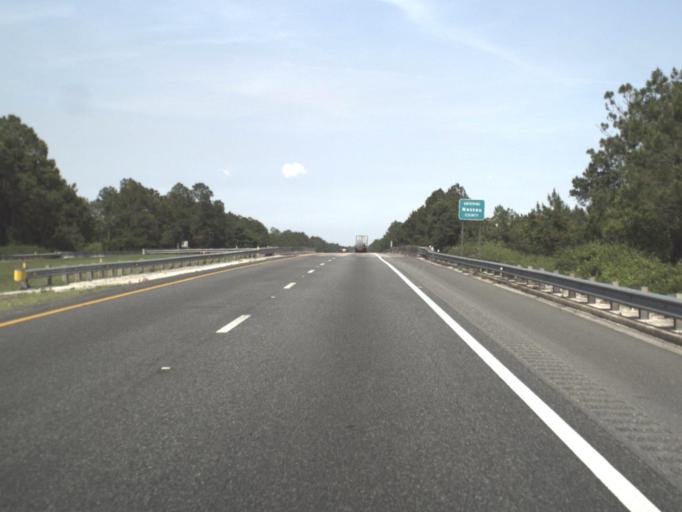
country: US
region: Florida
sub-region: Baker County
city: Macclenny
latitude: 30.2811
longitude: -82.0508
